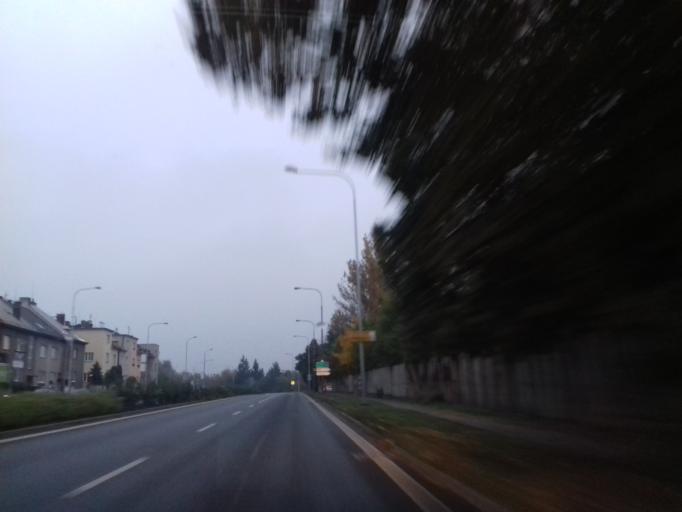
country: CZ
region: Olomoucky
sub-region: Okres Olomouc
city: Olomouc
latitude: 49.5972
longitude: 17.2318
